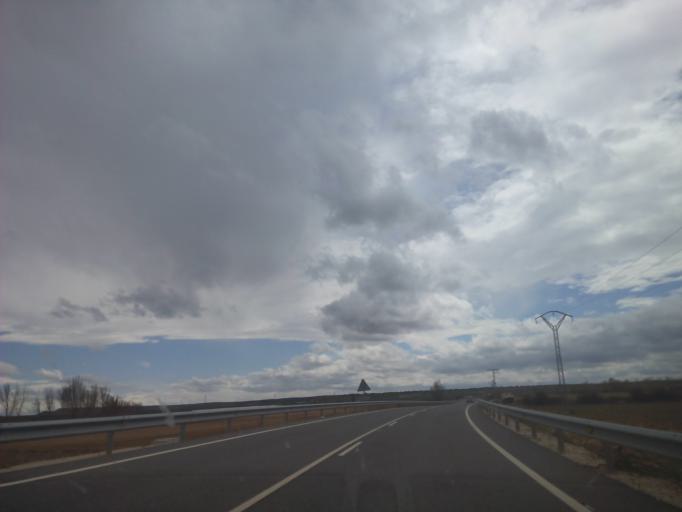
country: ES
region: Castille and Leon
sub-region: Provincia de Salamanca
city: Machacon
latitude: 40.9336
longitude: -5.4979
